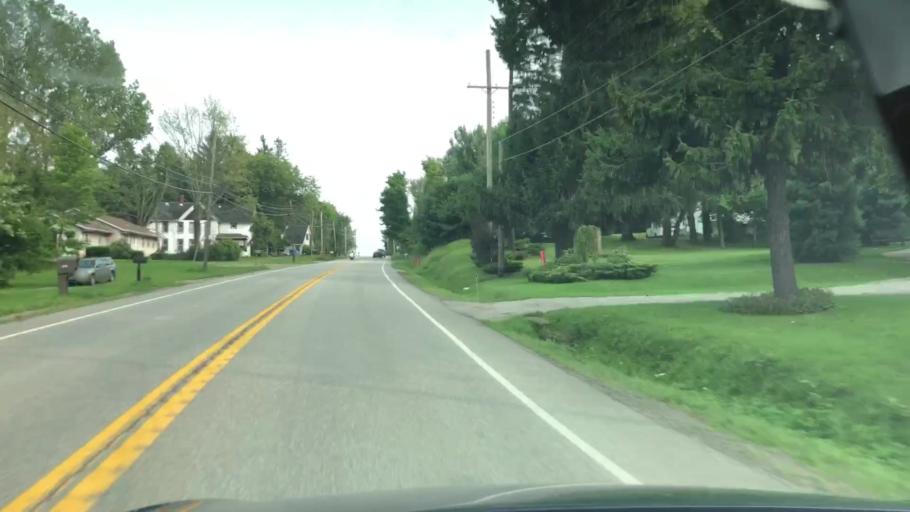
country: US
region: Pennsylvania
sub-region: Erie County
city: Wesleyville
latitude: 42.0829
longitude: -79.9921
